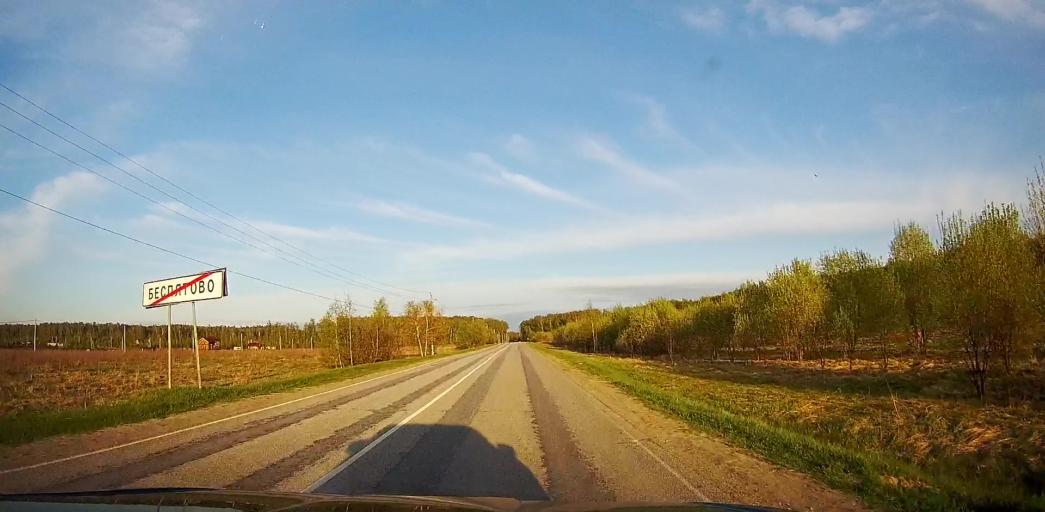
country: RU
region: Moskovskaya
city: Meshcherino
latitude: 55.2301
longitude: 38.3770
